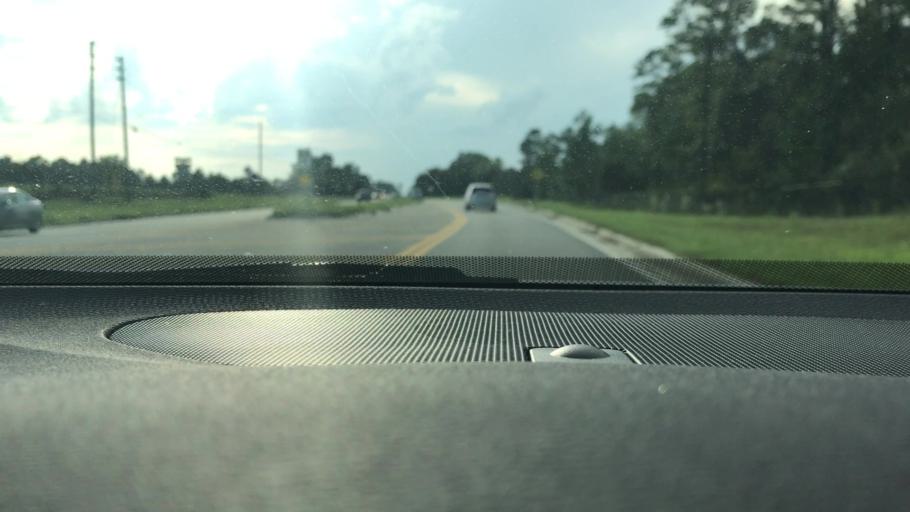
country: US
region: Florida
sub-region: Volusia County
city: Lake Helen
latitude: 28.9849
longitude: -81.2524
